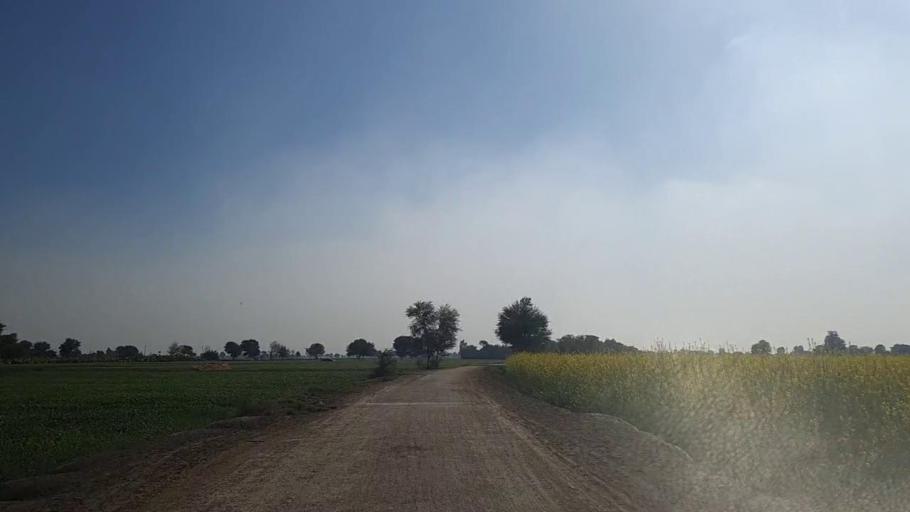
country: PK
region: Sindh
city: Shahpur Chakar
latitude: 26.2013
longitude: 68.6138
